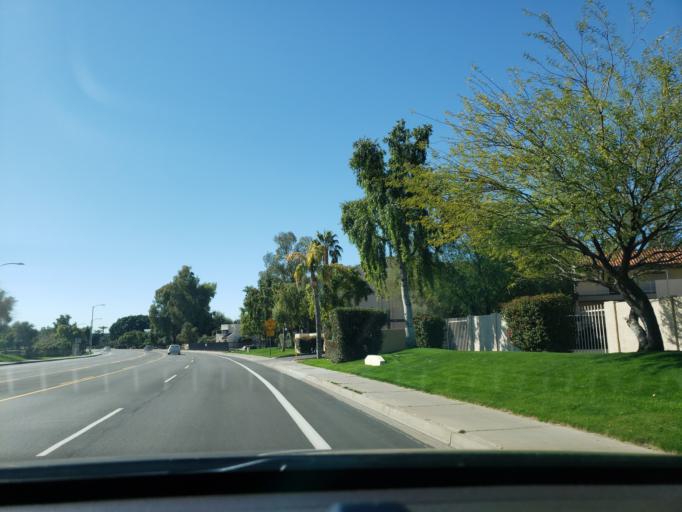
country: US
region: Arizona
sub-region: Maricopa County
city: Glendale
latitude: 33.5892
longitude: -112.1208
